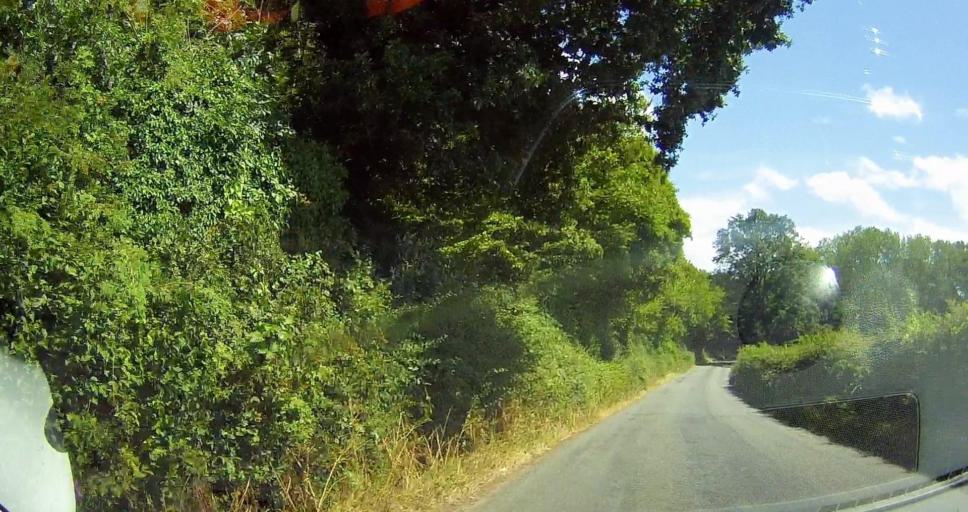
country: GB
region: England
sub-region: Kent
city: Borough Green
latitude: 51.2478
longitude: 0.3008
